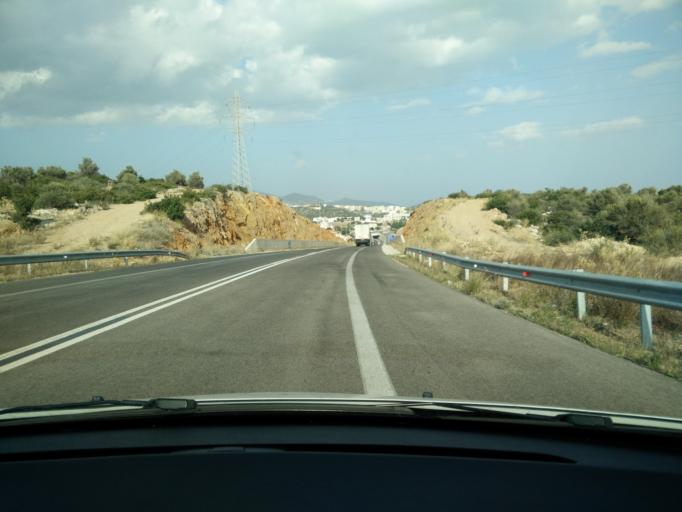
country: GR
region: Crete
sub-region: Nomos Lasithiou
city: Agios Nikolaos
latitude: 35.1786
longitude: 25.7013
